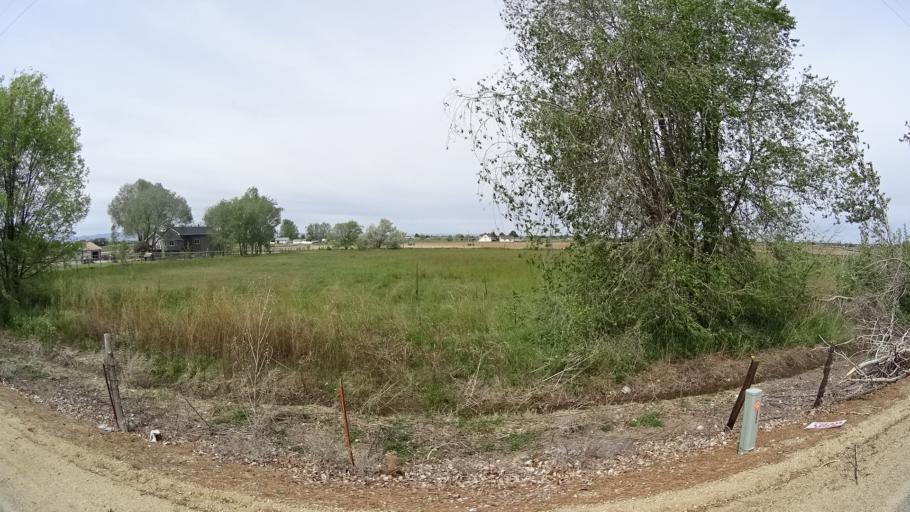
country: US
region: Idaho
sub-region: Ada County
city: Kuna
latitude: 43.5484
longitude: -116.4737
